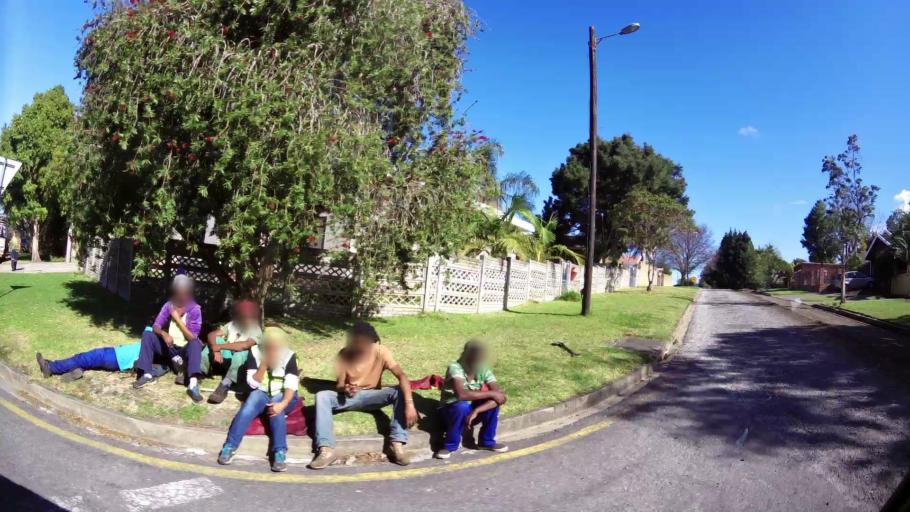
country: ZA
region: Western Cape
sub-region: Eden District Municipality
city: George
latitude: -33.9418
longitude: 22.4772
